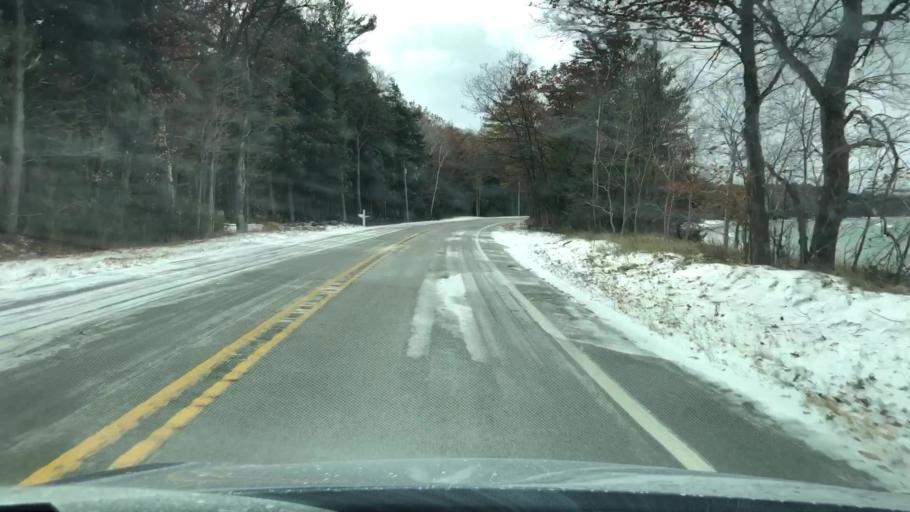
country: US
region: Michigan
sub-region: Antrim County
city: Elk Rapids
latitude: 44.9834
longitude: -85.4962
